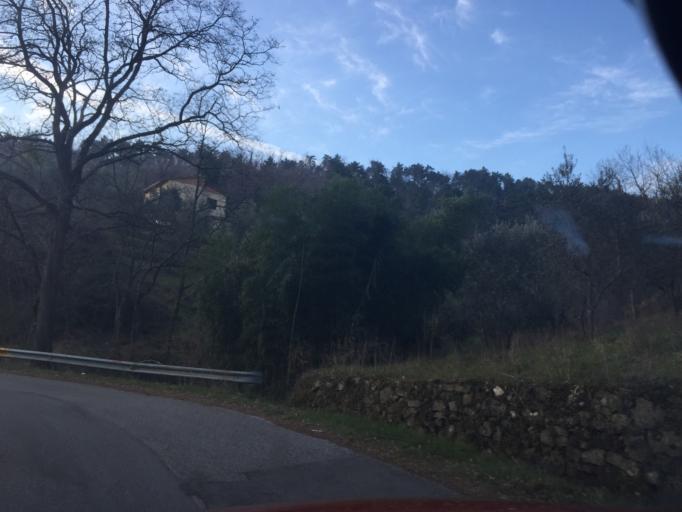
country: IT
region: Tuscany
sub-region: Provincia di Pistoia
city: Cantagrillo-Casalguidi
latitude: 43.8370
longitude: 10.9263
